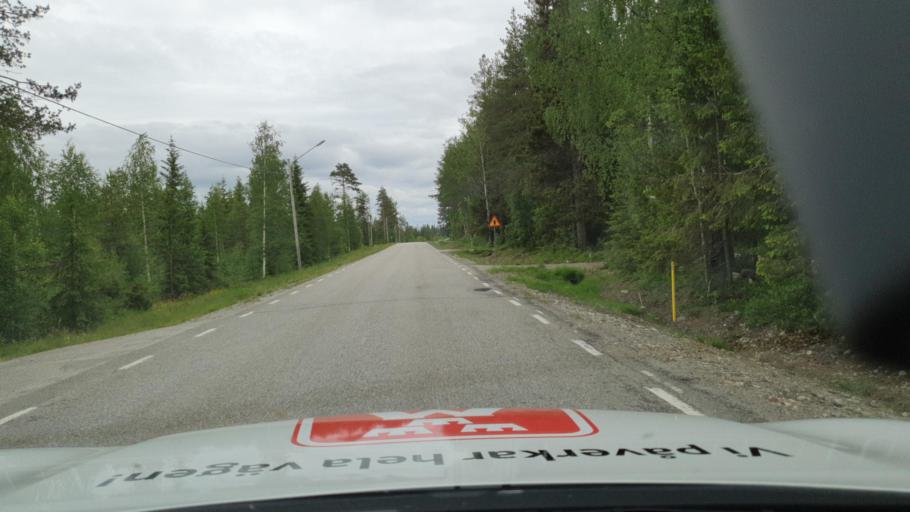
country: SE
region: Vaesterbotten
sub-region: Lycksele Kommun
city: Soderfors
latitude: 64.2939
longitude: 18.1781
